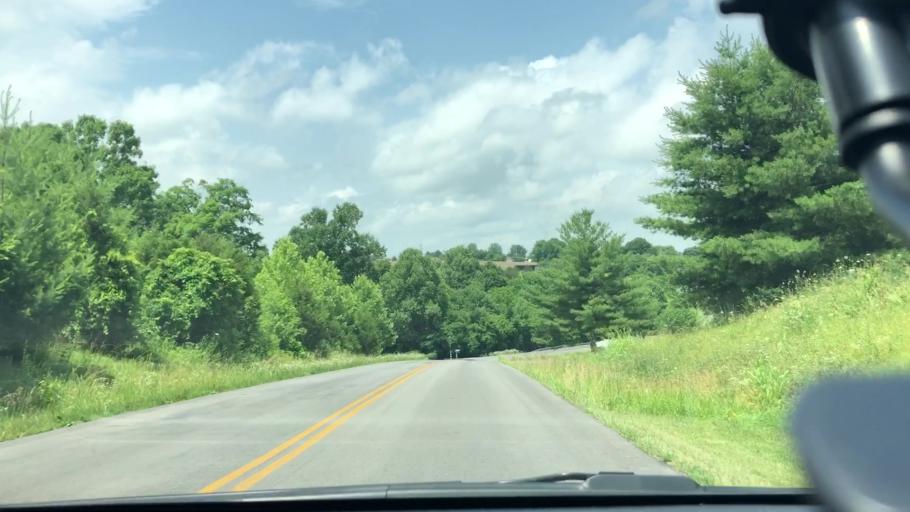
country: US
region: Kentucky
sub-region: Pulaski County
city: Somerset
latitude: 37.0585
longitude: -84.6607
